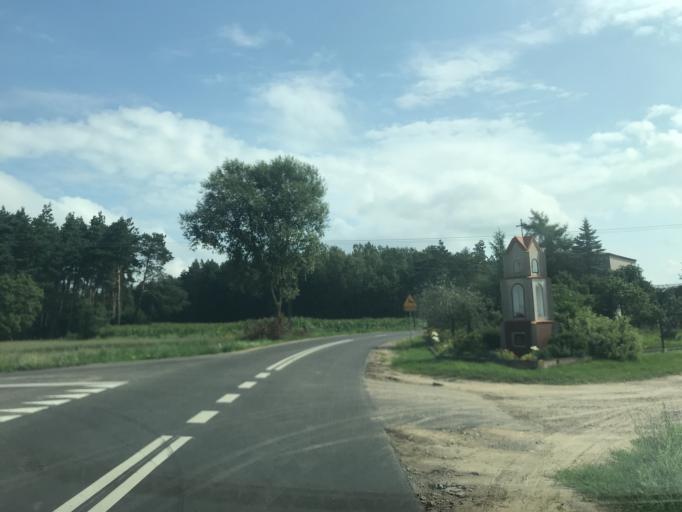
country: PL
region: Warmian-Masurian Voivodeship
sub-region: Powiat nowomiejski
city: Kurzetnik
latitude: 53.3979
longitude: 19.4721
